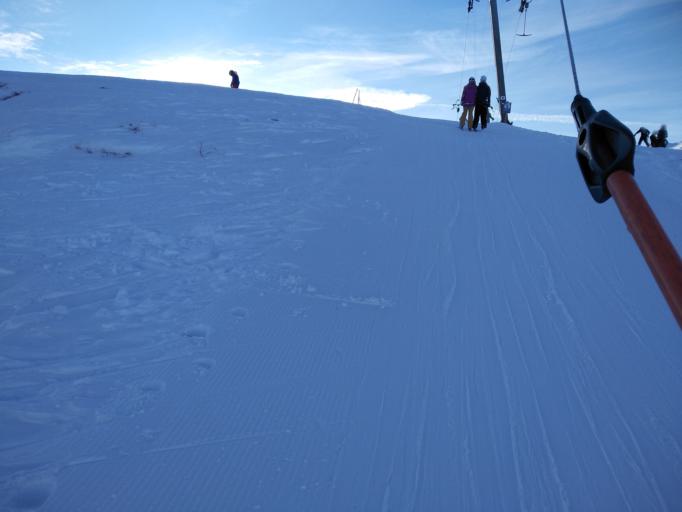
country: NO
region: Rogaland
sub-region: Suldal
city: Sand
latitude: 59.6144
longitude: 6.2253
